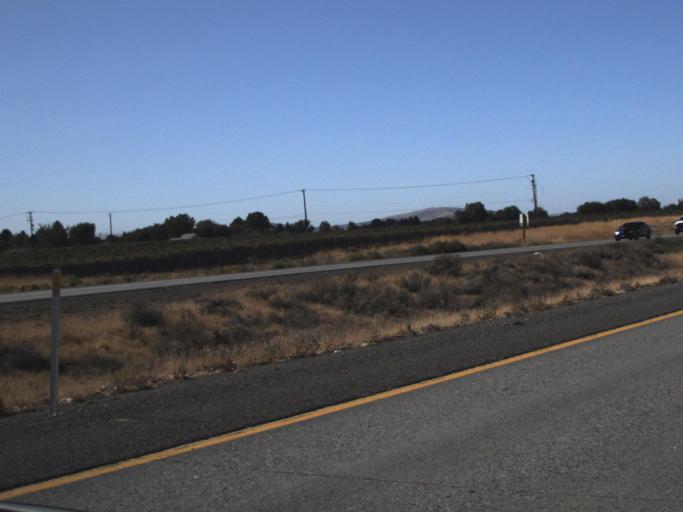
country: US
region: Washington
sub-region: Franklin County
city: Pasco
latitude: 46.2511
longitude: -119.1347
